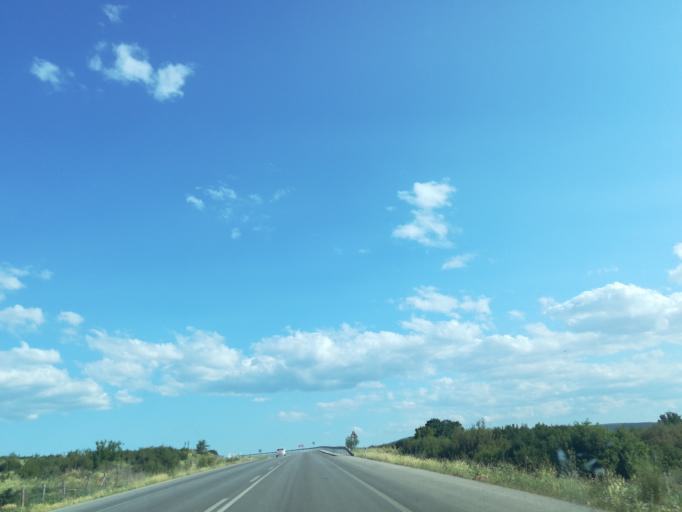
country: TR
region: Denizli
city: Ishakli
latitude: 38.1695
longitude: 30.0709
